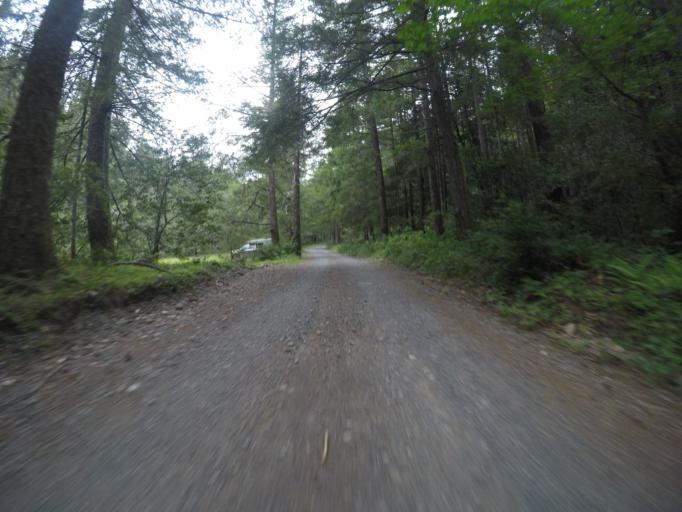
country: US
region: California
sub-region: Del Norte County
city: Bertsch-Oceanview
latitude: 41.7327
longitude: -123.8848
